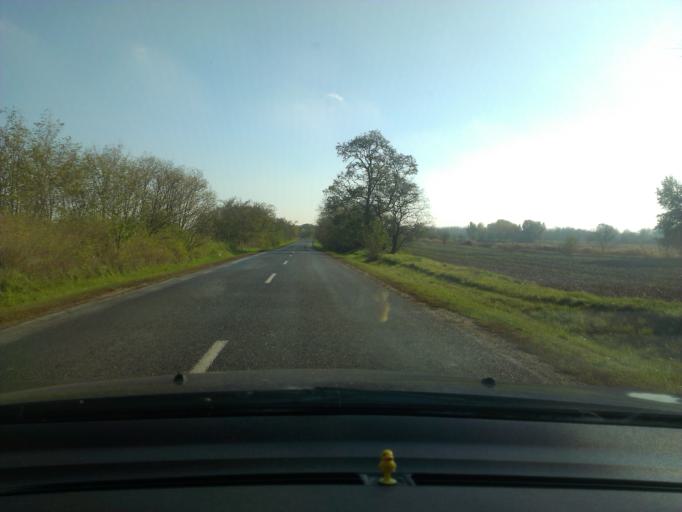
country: HU
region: Komarom-Esztergom
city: Mocsa
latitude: 47.7218
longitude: 18.1714
